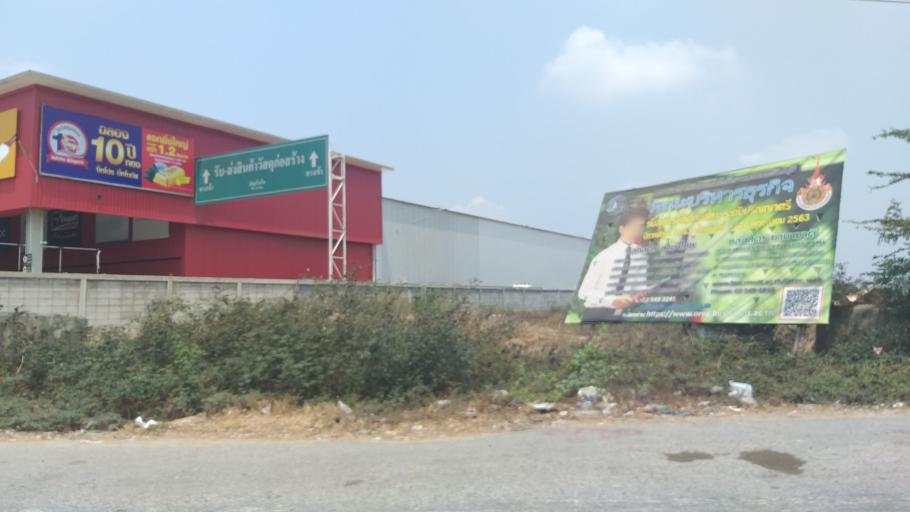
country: TH
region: Pathum Thani
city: Lam Luk Ka
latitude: 13.9369
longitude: 100.7541
